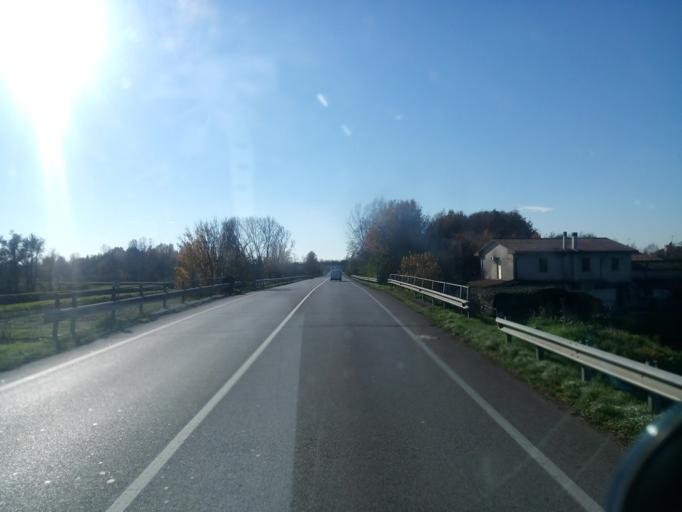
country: IT
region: Veneto
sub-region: Provincia di Padova
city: Campodarsego
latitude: 45.5075
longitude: 11.9328
